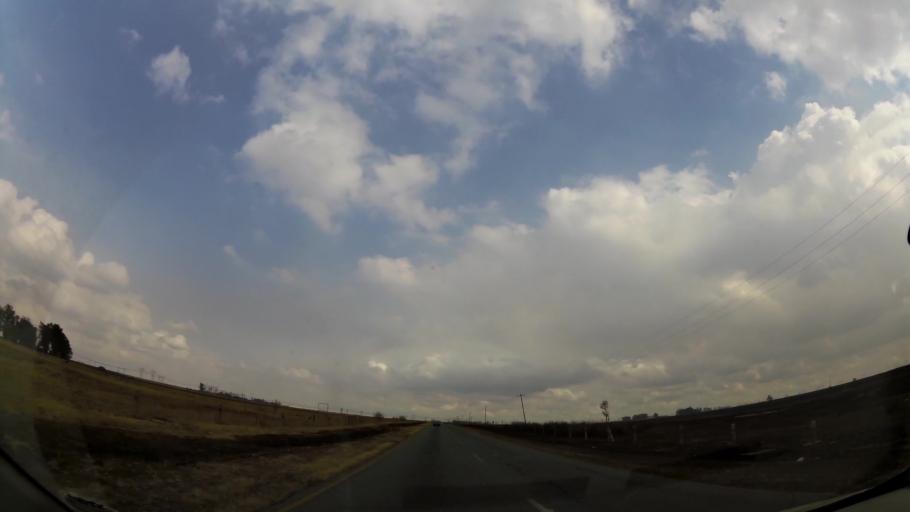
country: ZA
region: Orange Free State
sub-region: Fezile Dabi District Municipality
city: Sasolburg
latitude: -26.8066
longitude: 27.9127
